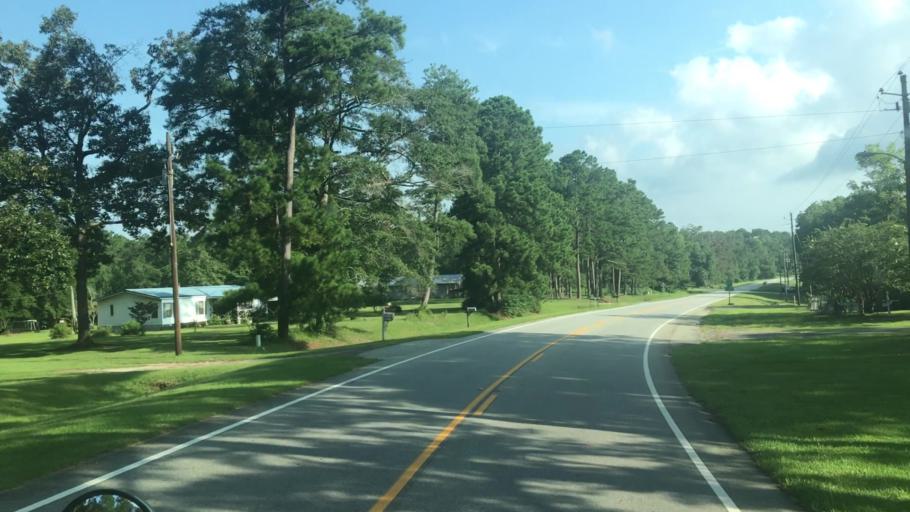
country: US
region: Florida
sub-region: Gadsden County
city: Havana
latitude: 30.7507
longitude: -84.4876
